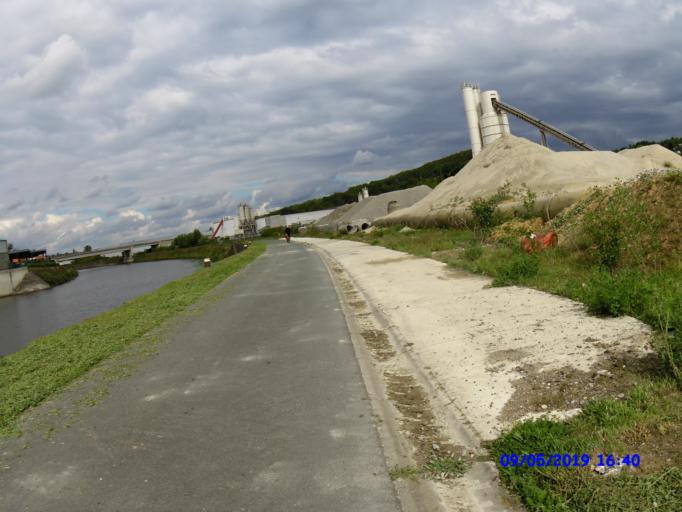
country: BE
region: Wallonia
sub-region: Province de Namur
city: Floreffe
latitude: 50.4435
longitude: 4.7885
